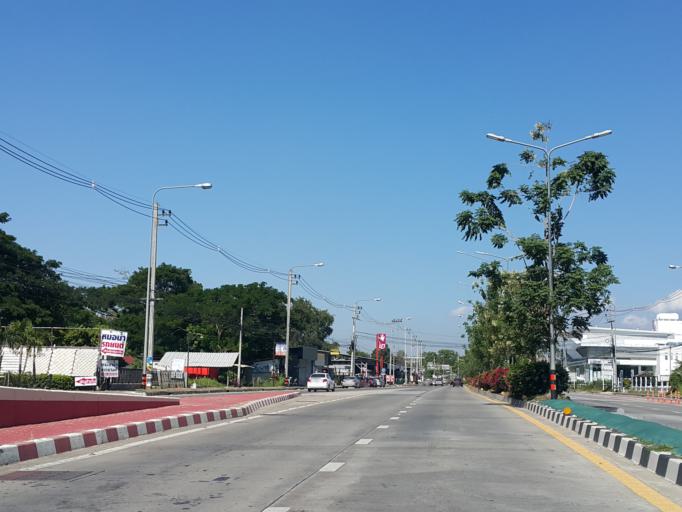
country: TH
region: Chiang Mai
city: Chiang Mai
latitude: 18.7819
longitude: 99.0420
